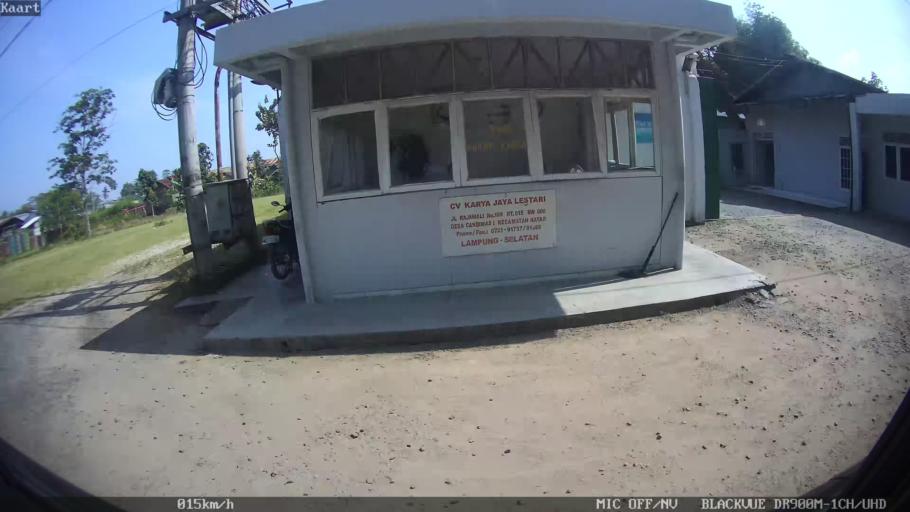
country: ID
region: Lampung
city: Natar
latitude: -5.2664
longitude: 105.1976
